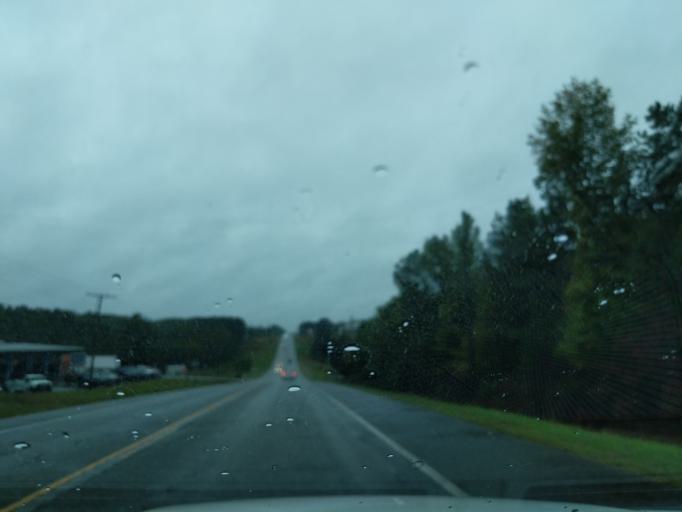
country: US
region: Louisiana
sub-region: Webster Parish
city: Minden
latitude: 32.6154
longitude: -93.2497
